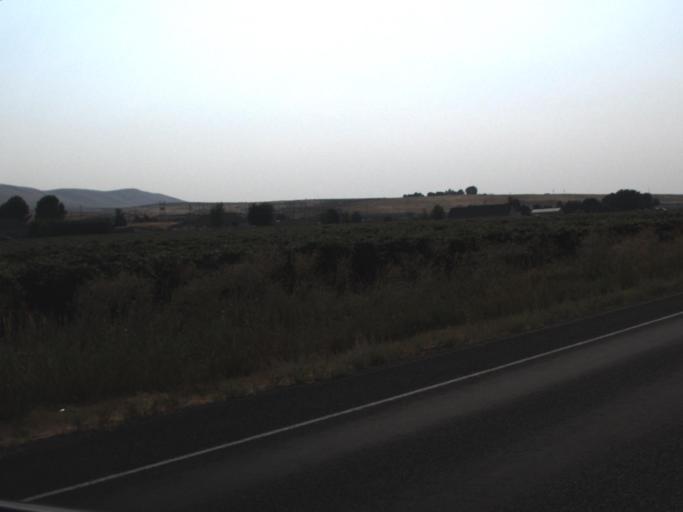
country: US
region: Washington
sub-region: Yakima County
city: Grandview
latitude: 46.1868
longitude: -119.8681
